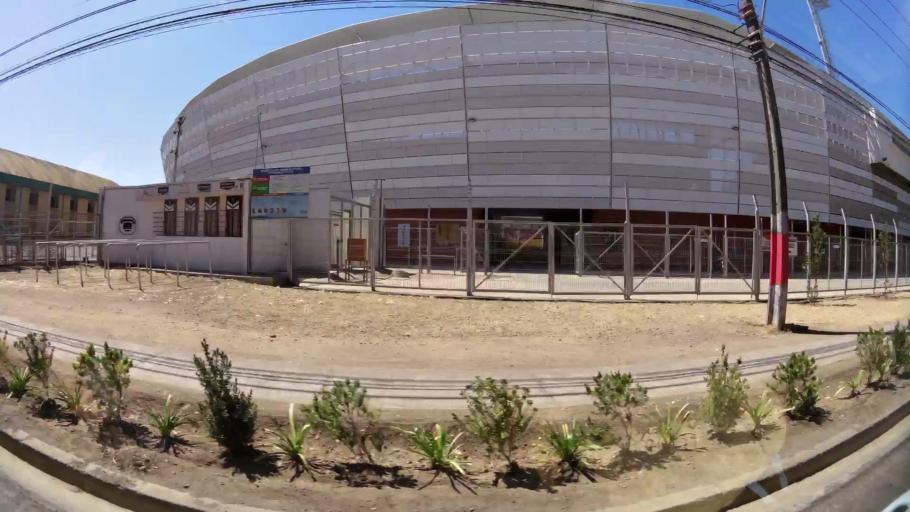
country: CL
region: Maule
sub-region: Provincia de Curico
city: Curico
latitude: -34.9735
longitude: -71.2315
